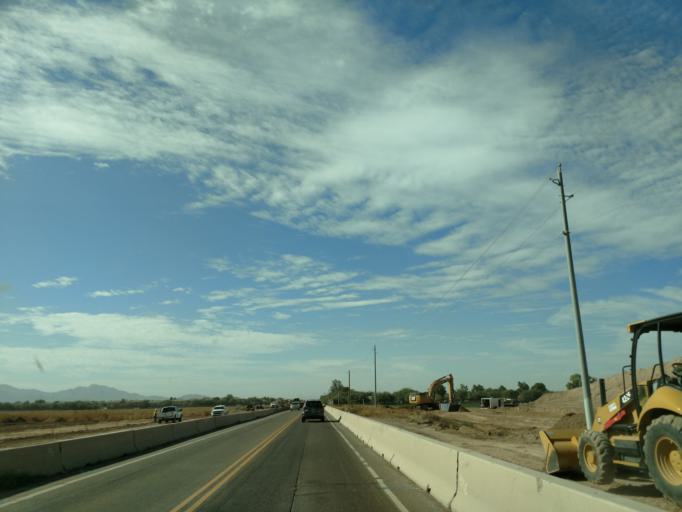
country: US
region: Arizona
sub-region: Maricopa County
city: Laveen
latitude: 33.3774
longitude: -112.1887
